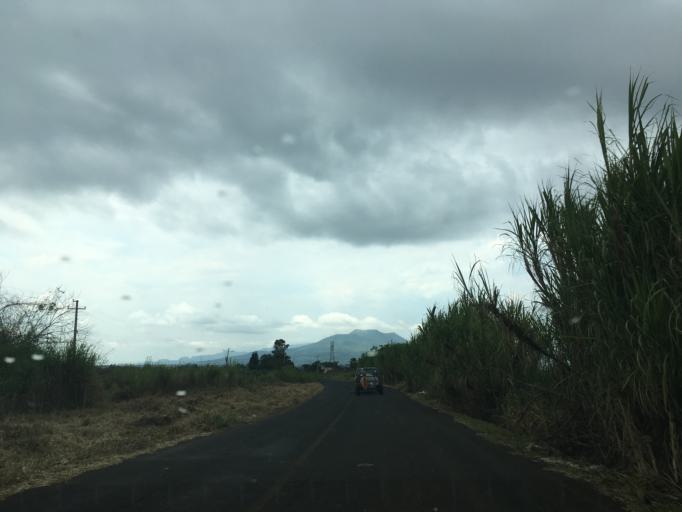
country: MX
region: Michoacan
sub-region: Periban
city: Gildardo Magana (Los Angeles)
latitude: 19.5801
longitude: -102.4481
